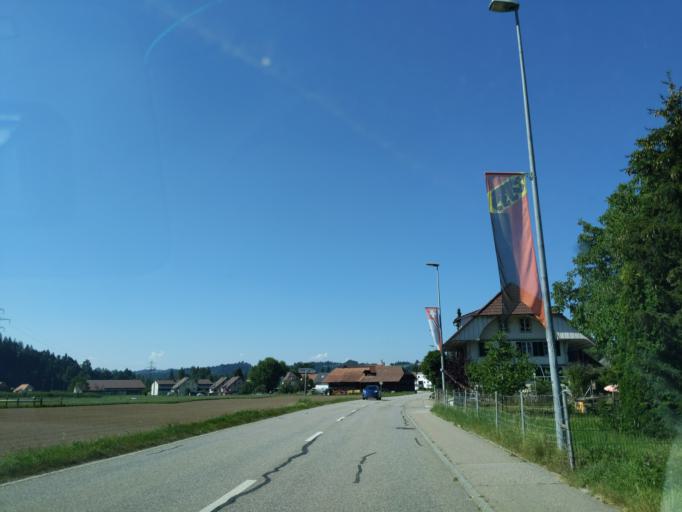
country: CH
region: Bern
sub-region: Emmental District
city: Lauperswil
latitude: 46.9708
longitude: 7.7404
